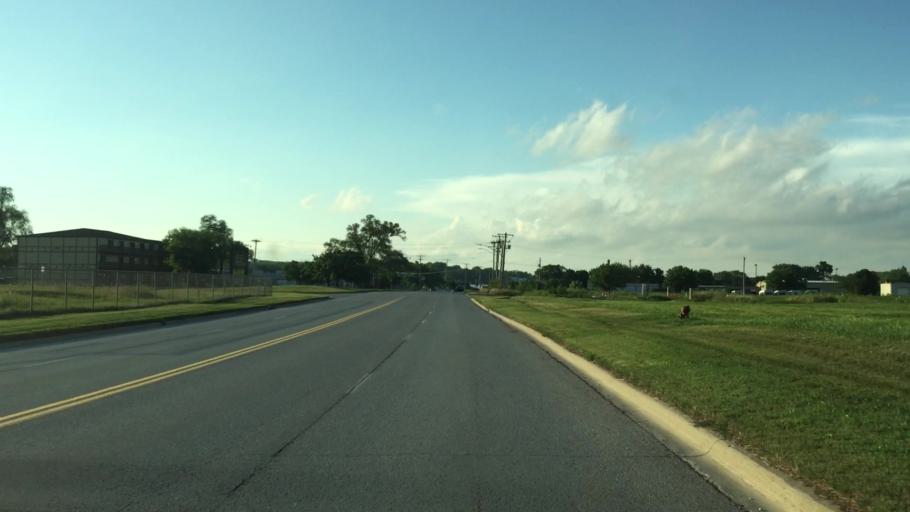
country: US
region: Iowa
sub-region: Johnson County
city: Iowa City
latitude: 41.6433
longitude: -91.5394
